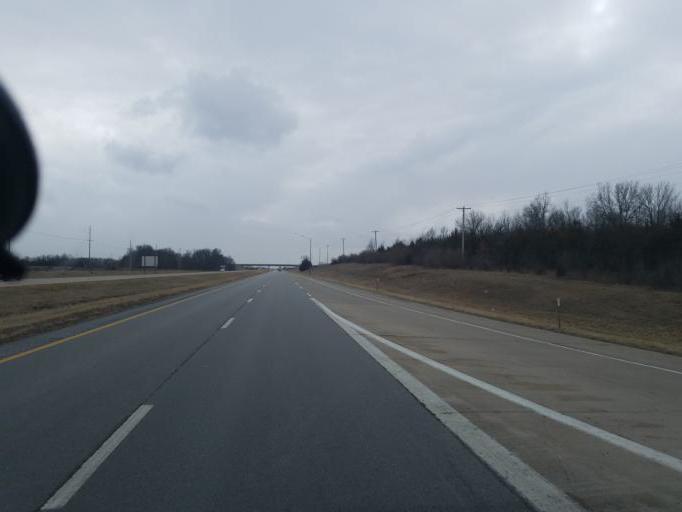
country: US
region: Missouri
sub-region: Randolph County
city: Moberly
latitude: 39.4151
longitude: -92.4123
